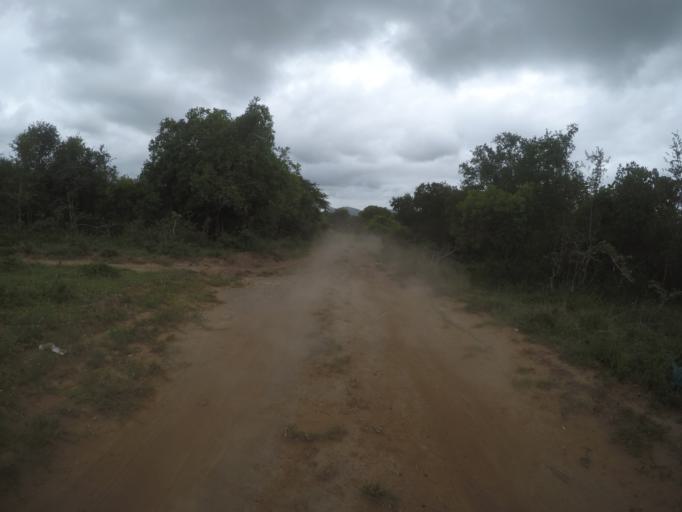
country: ZA
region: KwaZulu-Natal
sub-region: uThungulu District Municipality
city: Empangeni
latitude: -28.5923
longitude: 31.8416
